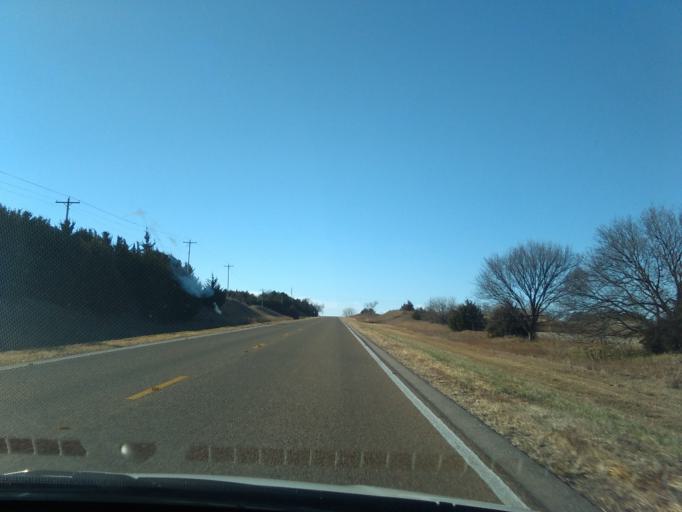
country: US
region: Nebraska
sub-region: Adams County
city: Hastings
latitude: 40.4373
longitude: -98.3666
